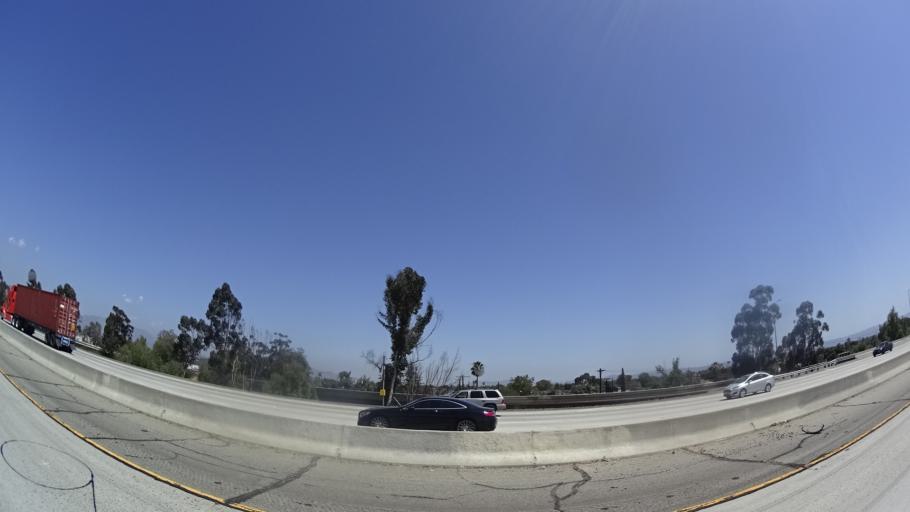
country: US
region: California
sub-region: Los Angeles County
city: San Fernando
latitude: 34.2714
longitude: -118.4306
